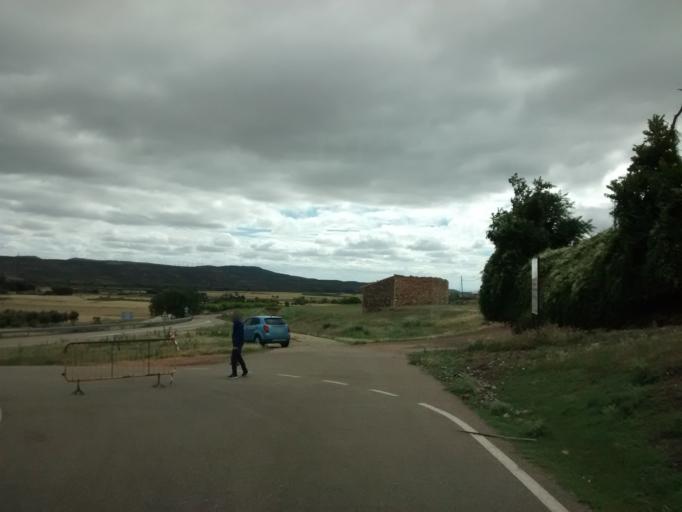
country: ES
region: Aragon
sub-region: Provincia de Zaragoza
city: Trasmoz
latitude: 41.8277
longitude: -1.7205
